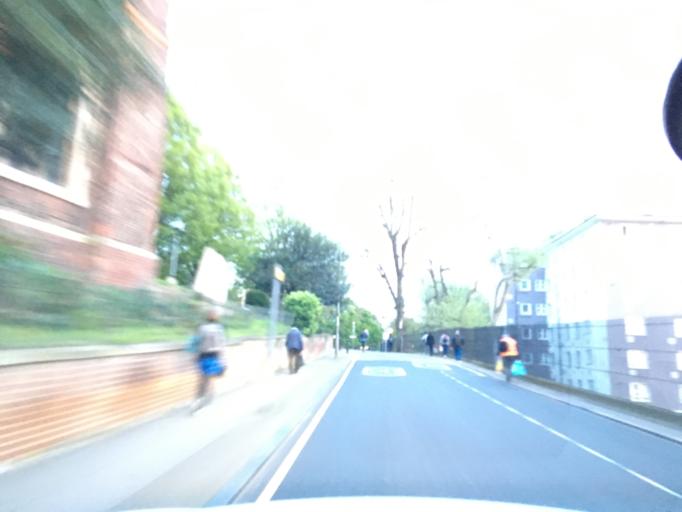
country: GB
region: England
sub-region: Greater London
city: Woolwich
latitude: 51.4819
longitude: 0.0353
